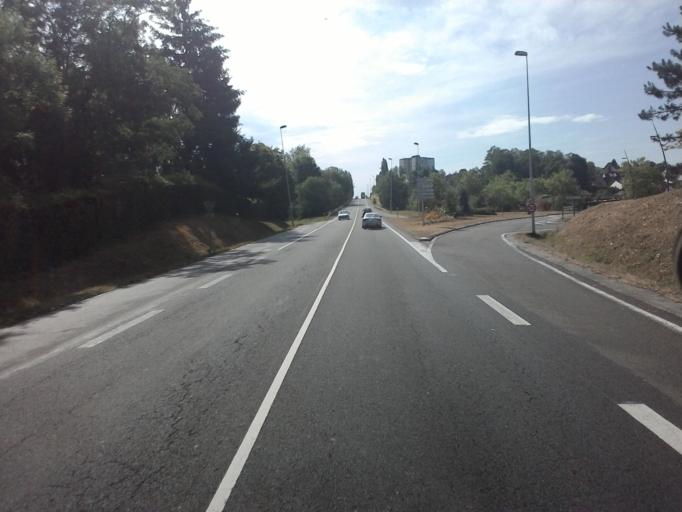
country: FR
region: Franche-Comte
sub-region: Departement du Jura
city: Lons-le-Saunier
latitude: 46.6853
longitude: 5.5662
